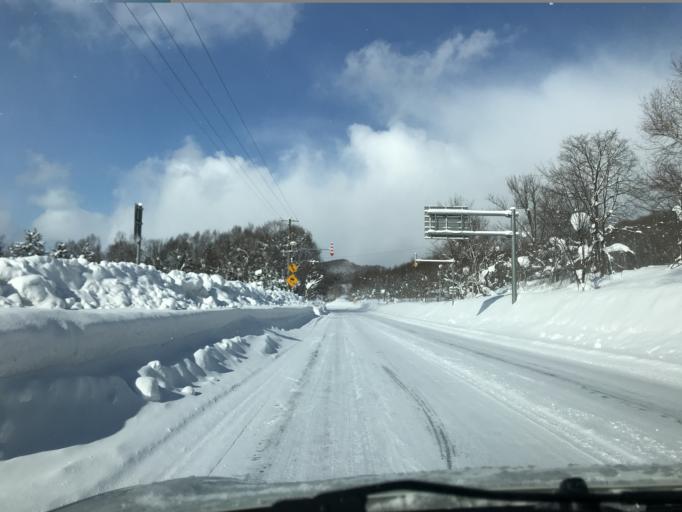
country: JP
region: Hokkaido
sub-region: Asahikawa-shi
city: Asahikawa
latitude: 43.9310
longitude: 142.4721
